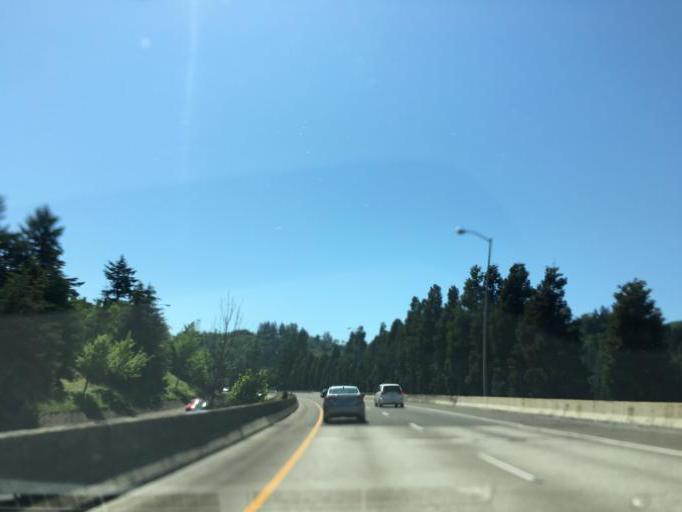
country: US
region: Oregon
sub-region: Multnomah County
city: Lents
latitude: 45.5473
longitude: -122.5551
